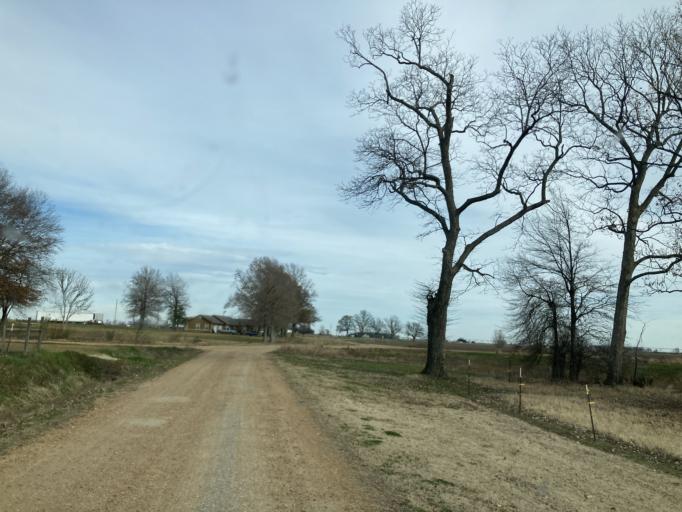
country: US
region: Mississippi
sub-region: Humphreys County
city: Belzoni
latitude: 33.1235
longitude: -90.6156
